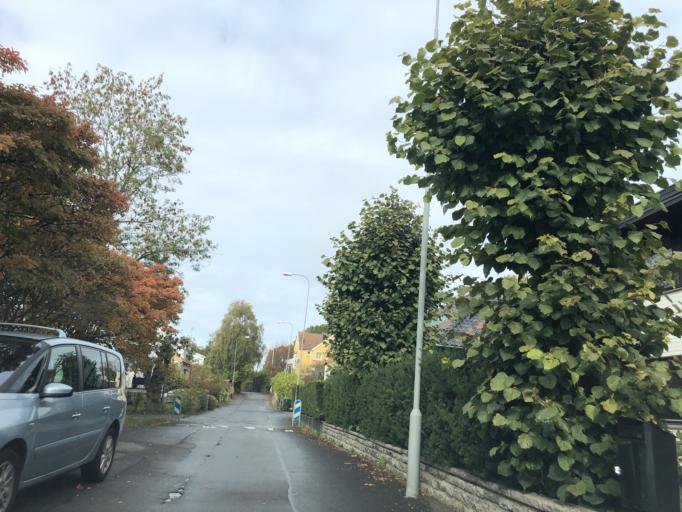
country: SE
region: Vaestra Goetaland
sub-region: Goteborg
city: Majorna
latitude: 57.6711
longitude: 11.8724
